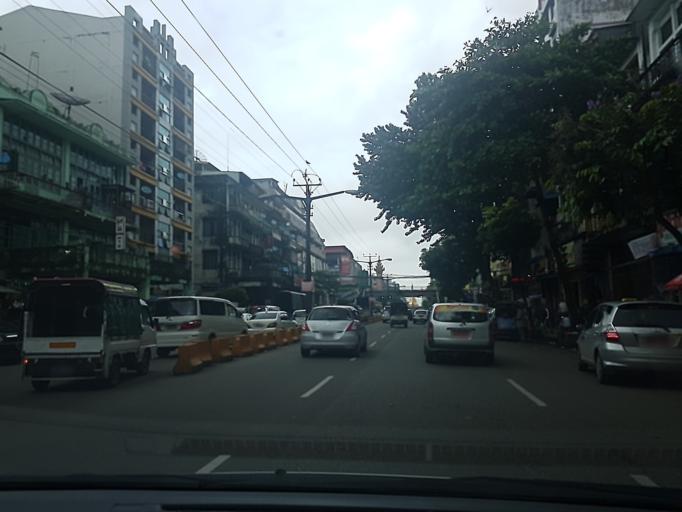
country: MM
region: Yangon
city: Yangon
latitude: 16.7747
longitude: 96.1517
